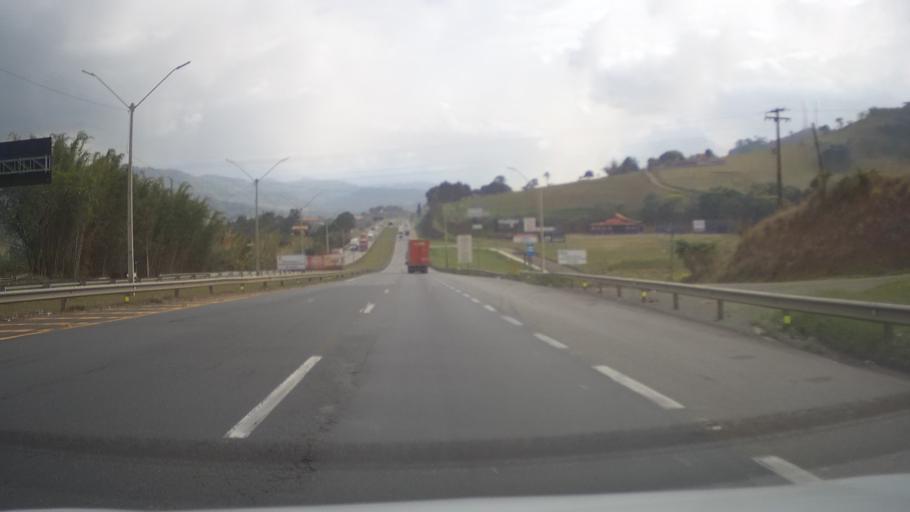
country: BR
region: Minas Gerais
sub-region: Extrema
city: Extrema
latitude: -22.9061
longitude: -46.4228
